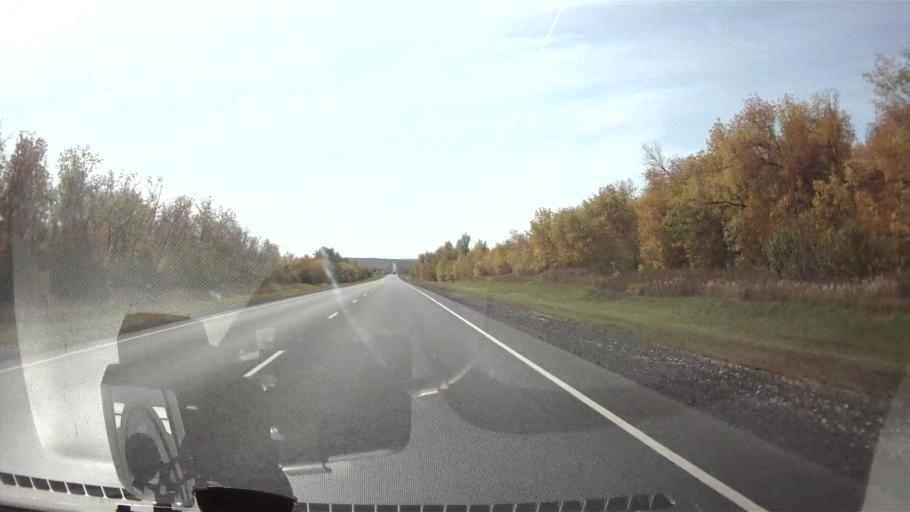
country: RU
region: Saratov
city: Khvalynsk
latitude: 52.5934
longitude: 48.1340
